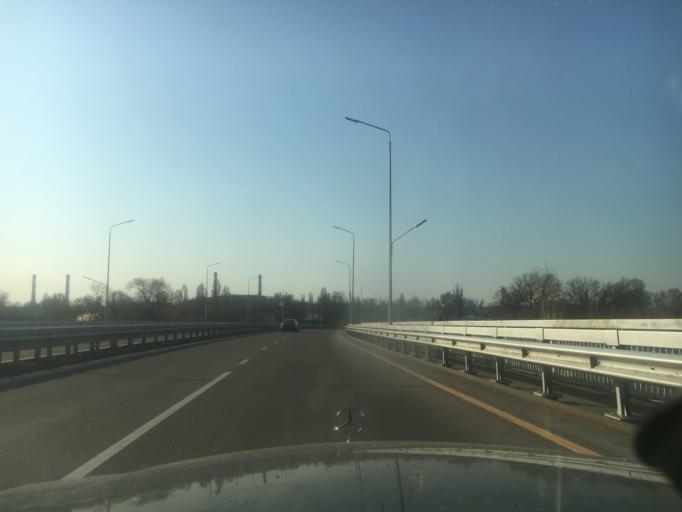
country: KZ
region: Almaty Qalasy
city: Almaty
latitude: 43.2765
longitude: 76.9440
